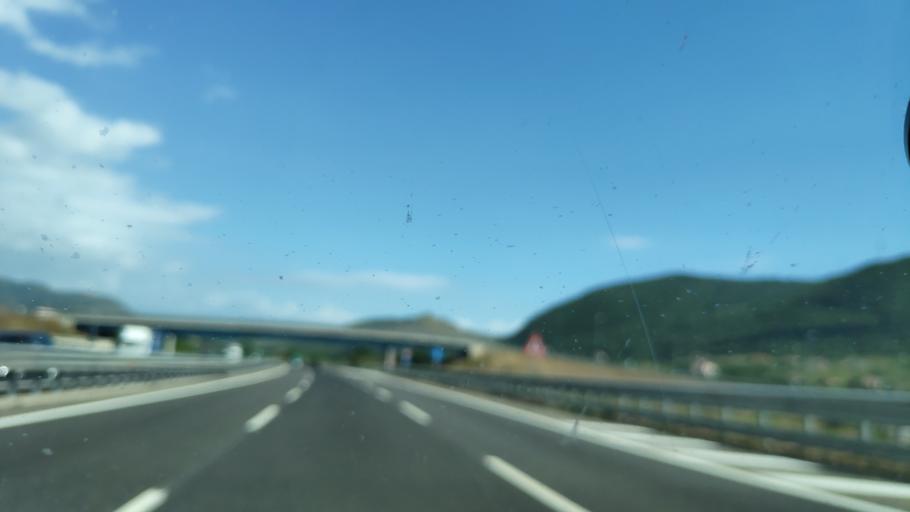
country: IT
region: Campania
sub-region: Provincia di Salerno
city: San Mango Piemonte
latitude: 40.6901
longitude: 14.8383
